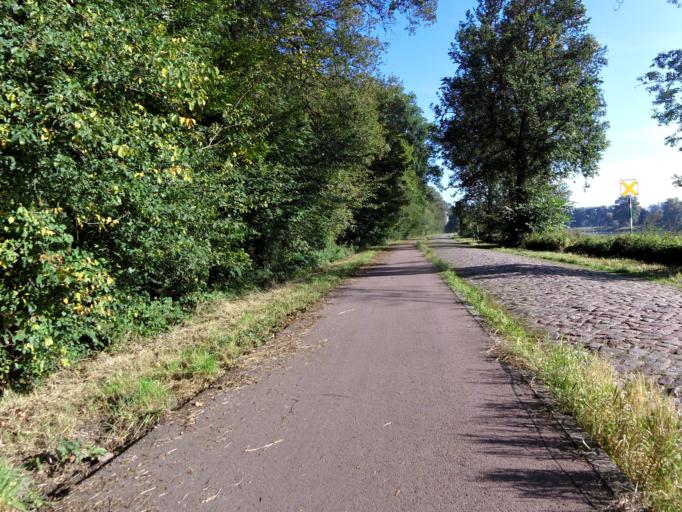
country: DE
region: Saxony-Anhalt
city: Coswig
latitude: 51.8730
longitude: 12.4481
